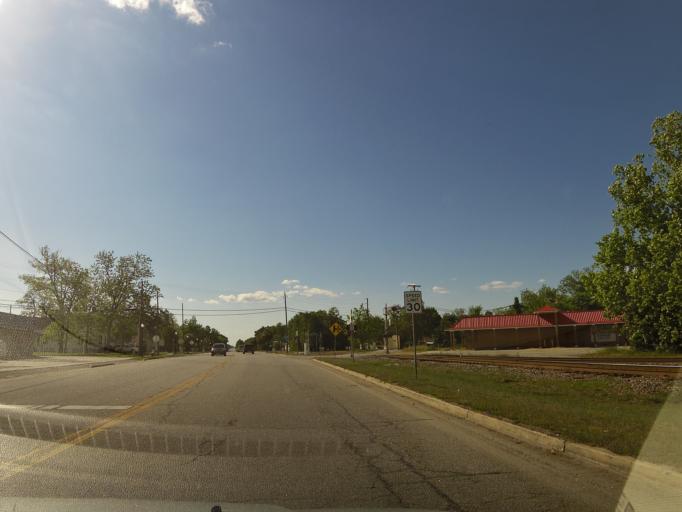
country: US
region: South Carolina
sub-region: Allendale County
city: Fairfax
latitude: 32.9592
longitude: -81.2374
